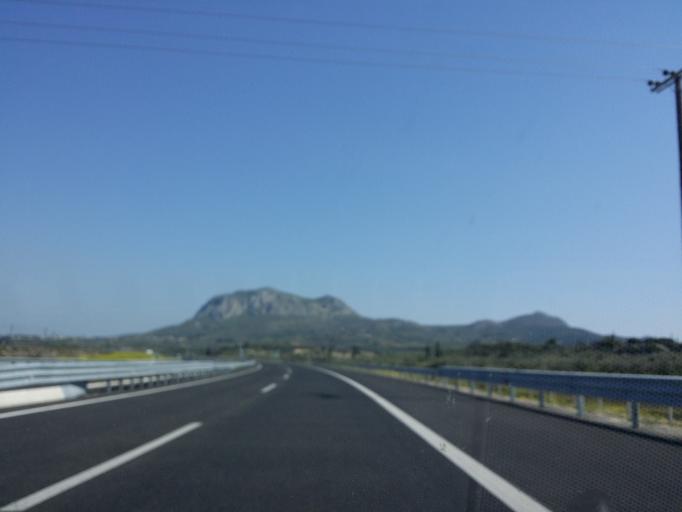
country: GR
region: Peloponnese
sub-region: Nomos Korinthias
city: Lekhaio
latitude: 37.9132
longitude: 22.8318
